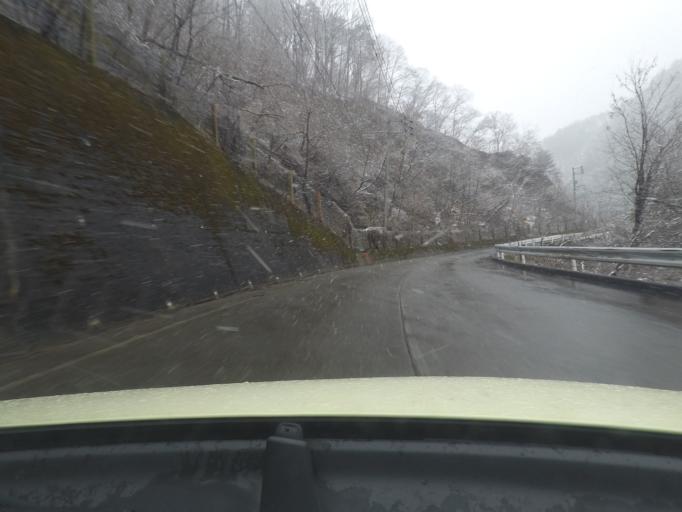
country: JP
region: Gifu
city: Takayama
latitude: 36.1344
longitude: 137.3239
